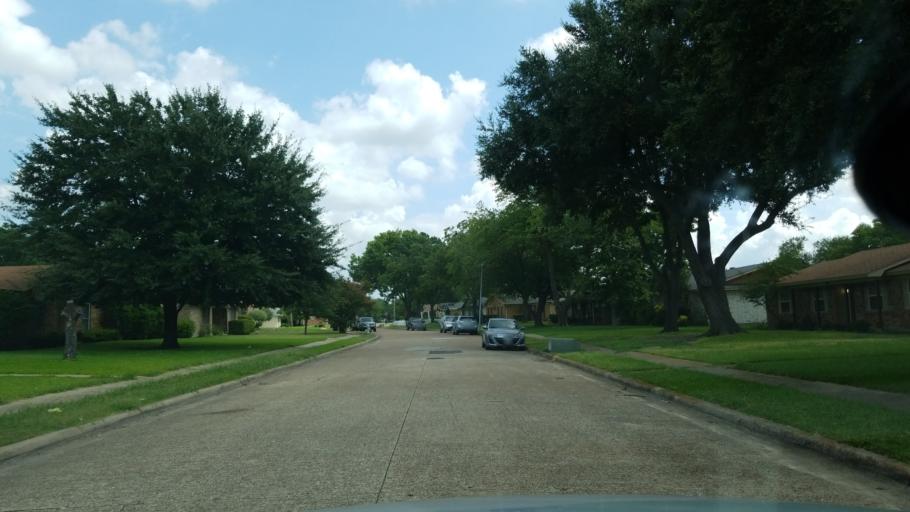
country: US
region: Texas
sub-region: Dallas County
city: Garland
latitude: 32.9260
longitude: -96.6505
